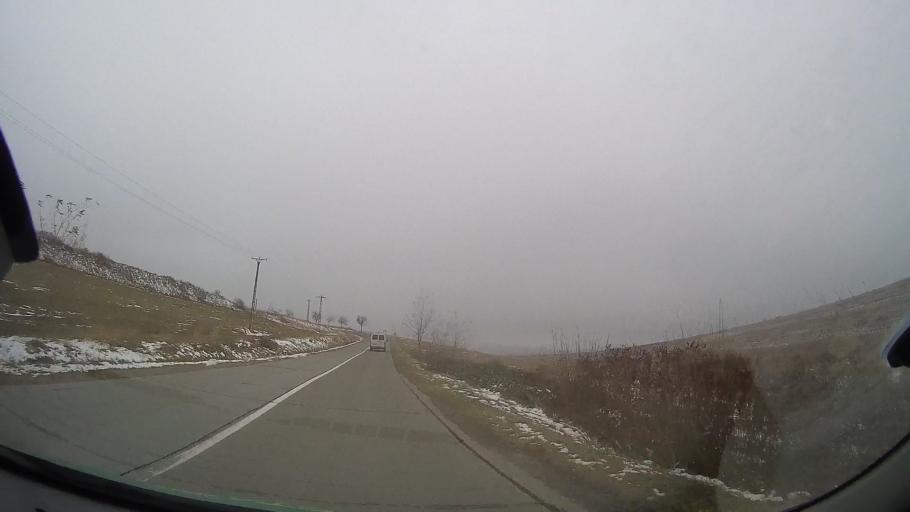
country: RO
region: Vaslui
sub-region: Comuna Grivita
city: Grivita
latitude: 46.1966
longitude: 27.6079
